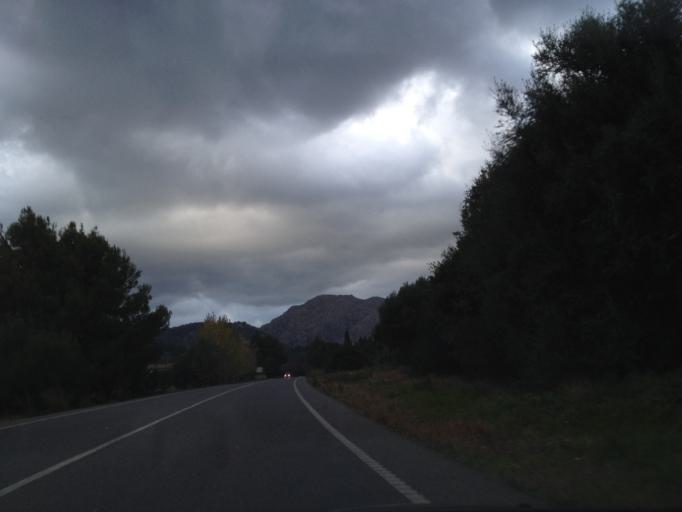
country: ES
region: Balearic Islands
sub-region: Illes Balears
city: Pollenca
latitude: 39.8660
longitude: 3.0143
